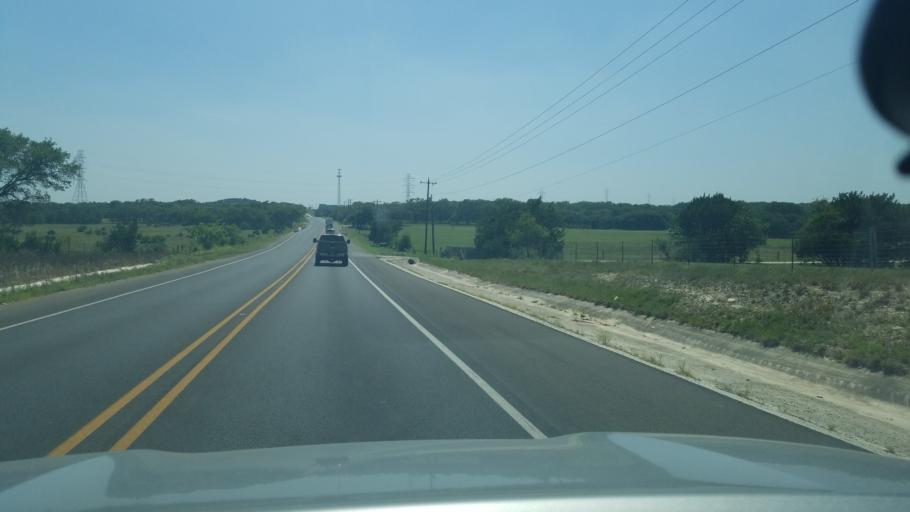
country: US
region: Texas
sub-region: Bexar County
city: Fair Oaks Ranch
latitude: 29.8054
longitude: -98.6544
